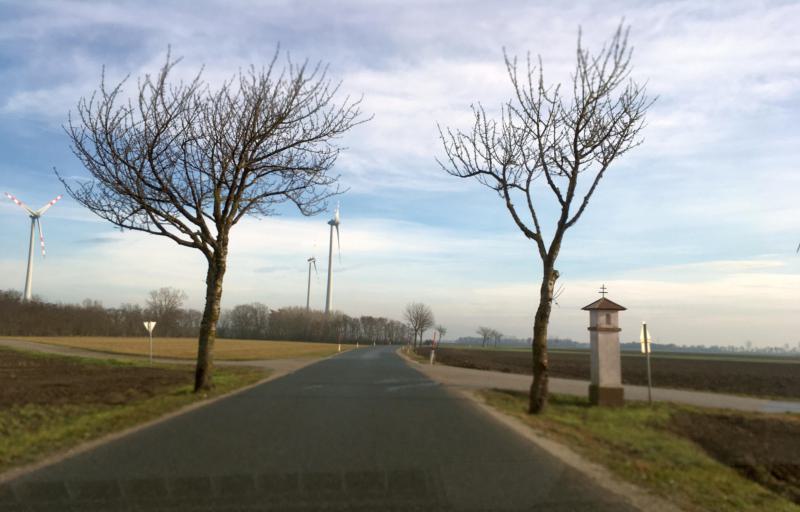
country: AT
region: Lower Austria
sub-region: Politischer Bezirk Ganserndorf
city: Andlersdorf
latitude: 48.1939
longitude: 16.6698
